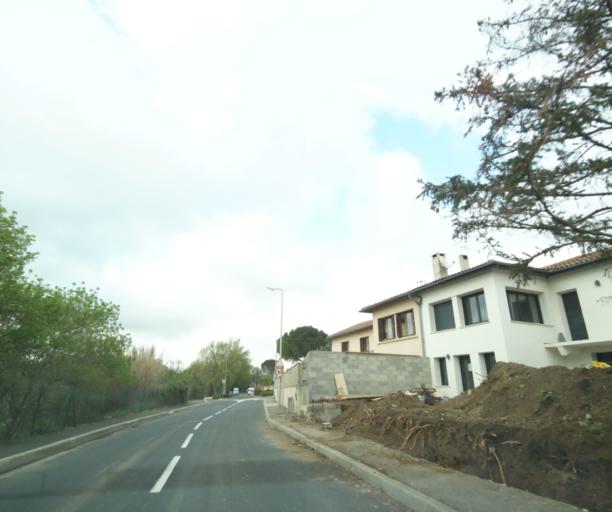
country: FR
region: Languedoc-Roussillon
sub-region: Departement de l'Herault
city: Saint-Jean-de-Vedas
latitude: 43.5771
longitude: 3.8172
